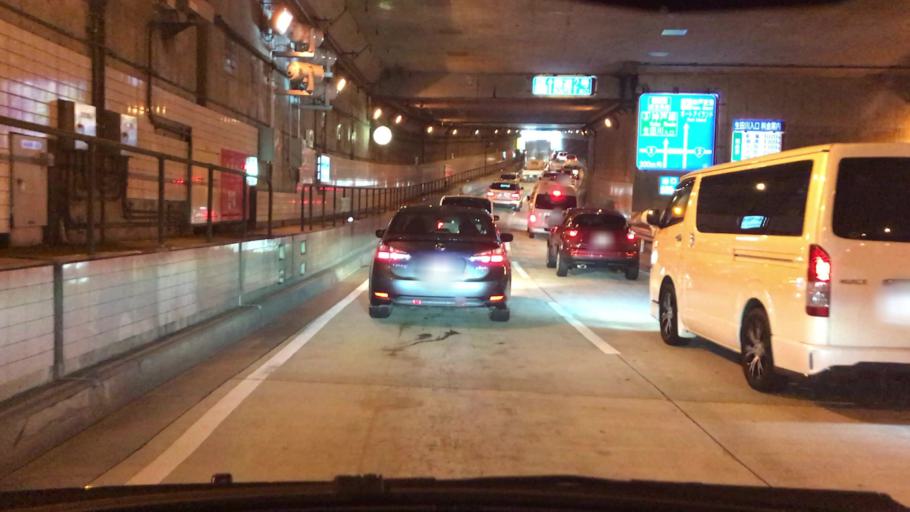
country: JP
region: Hyogo
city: Kobe
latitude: 34.7126
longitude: 135.1942
